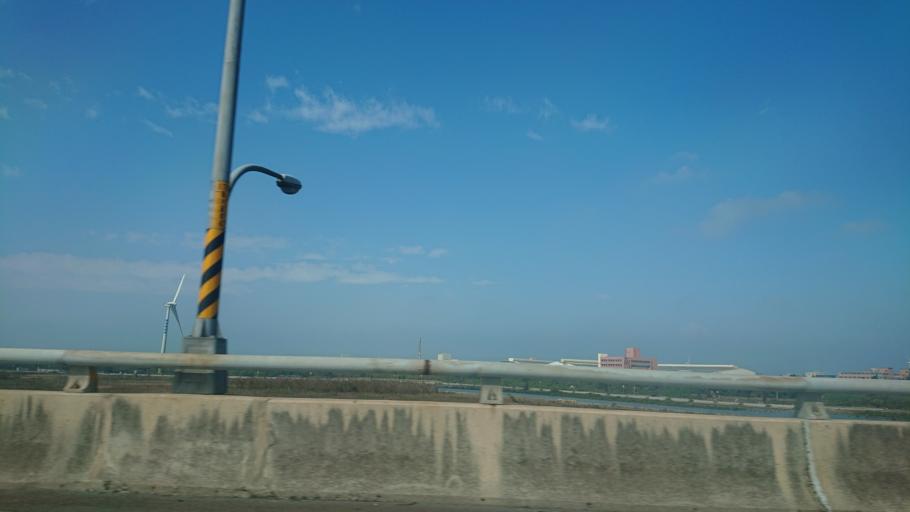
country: TW
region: Taiwan
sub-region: Changhua
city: Chang-hua
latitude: 24.0717
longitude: 120.4148
